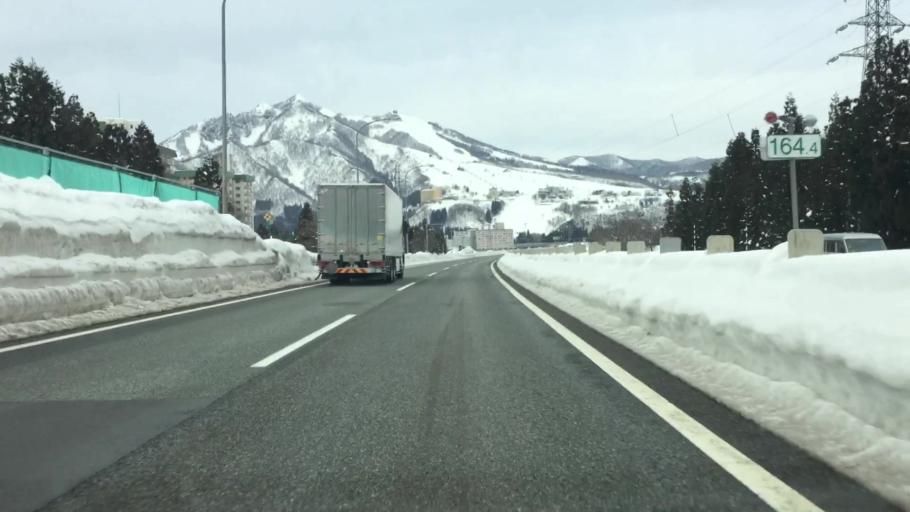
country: JP
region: Niigata
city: Shiozawa
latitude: 36.9148
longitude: 138.8395
